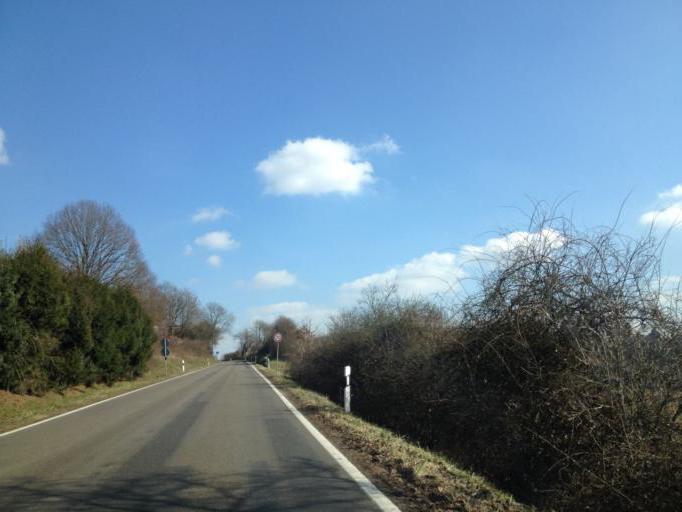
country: DE
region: Saarland
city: Sankt Wendel
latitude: 49.4679
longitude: 7.1886
